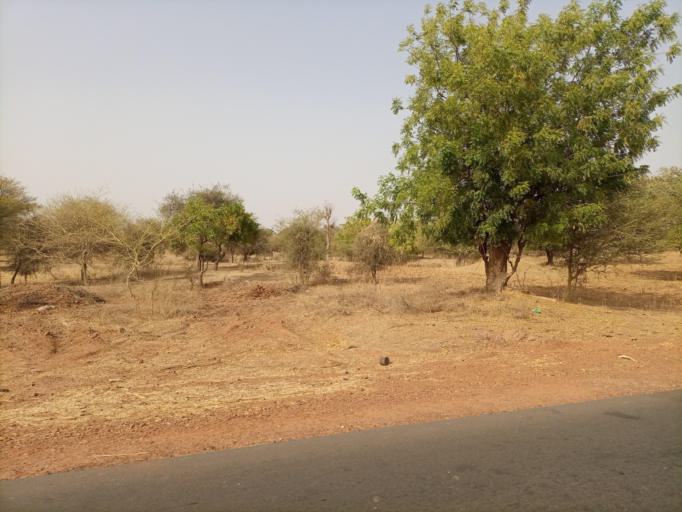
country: SN
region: Fatick
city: Foundiougne
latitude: 14.1187
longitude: -16.4505
